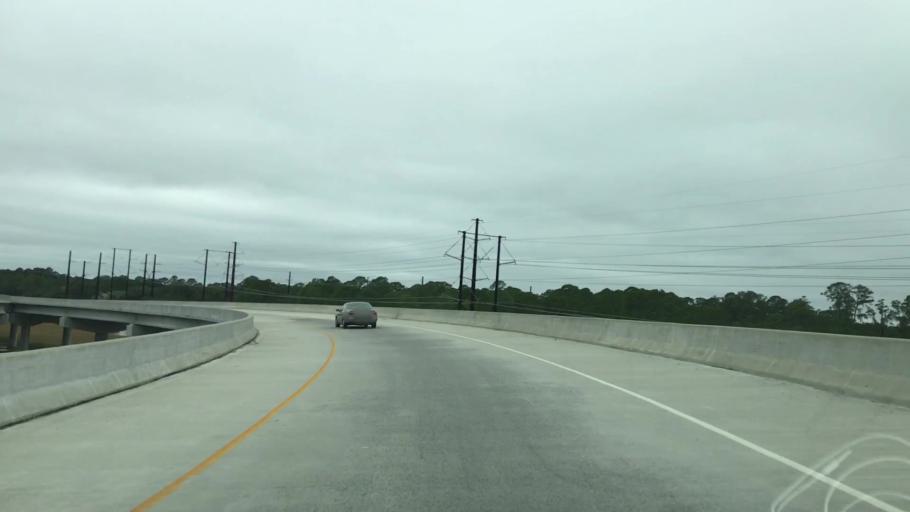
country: US
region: South Carolina
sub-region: Beaufort County
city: Hilton Head Island
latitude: 32.2348
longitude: -80.8034
